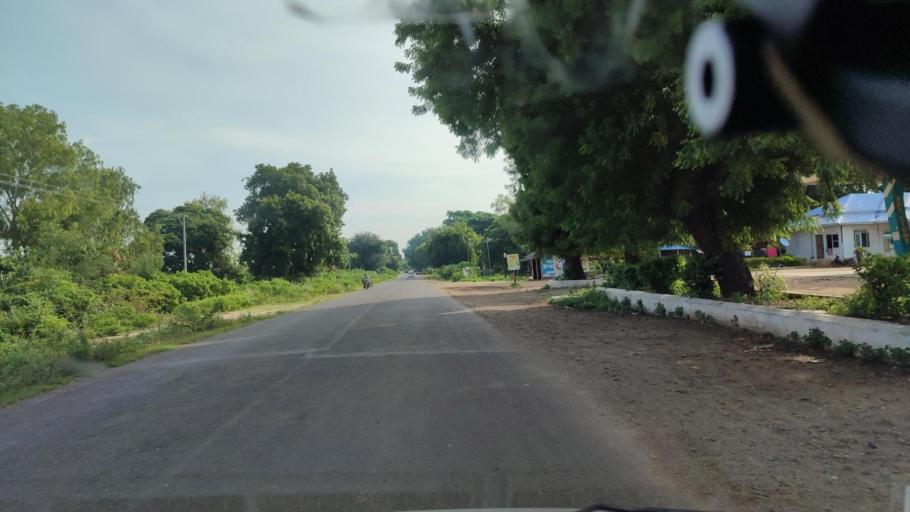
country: MM
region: Magway
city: Pakokku
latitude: 21.2599
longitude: 95.0407
